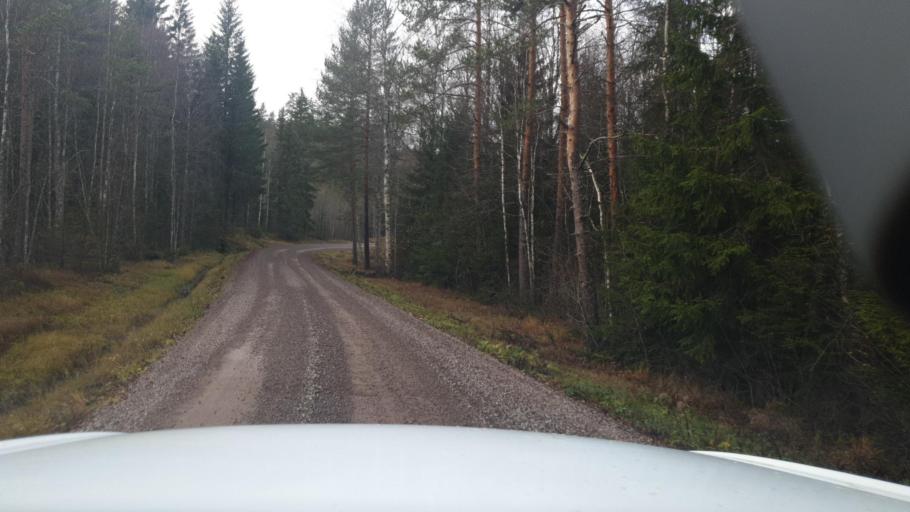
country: SE
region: Vaermland
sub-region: Eda Kommun
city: Charlottenberg
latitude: 60.0907
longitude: 12.5037
